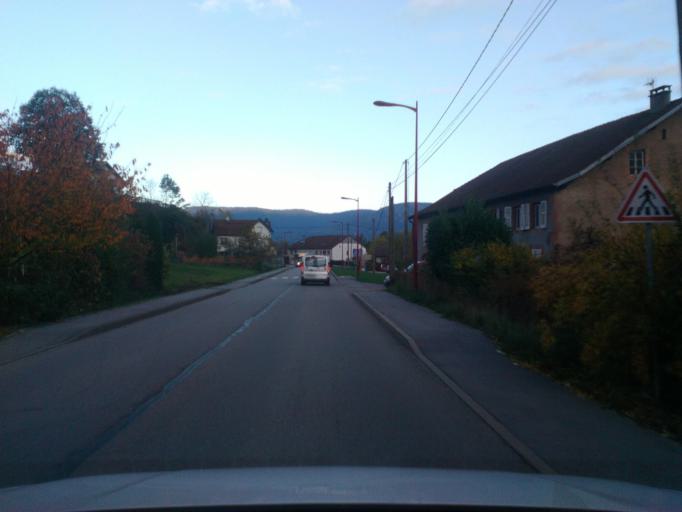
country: FR
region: Lorraine
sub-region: Departement des Vosges
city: Ban-de-Laveline
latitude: 48.2621
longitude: 7.0511
